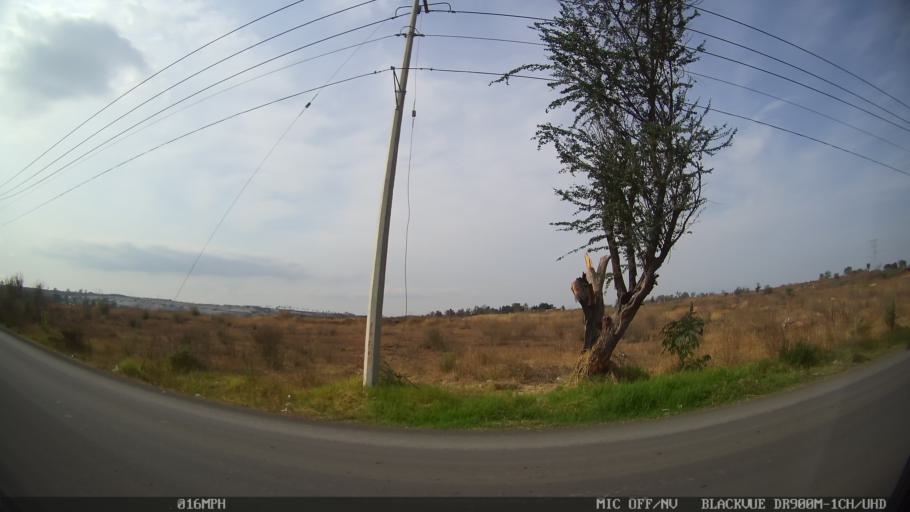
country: MX
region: Jalisco
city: Tonala
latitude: 20.6239
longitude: -103.2172
